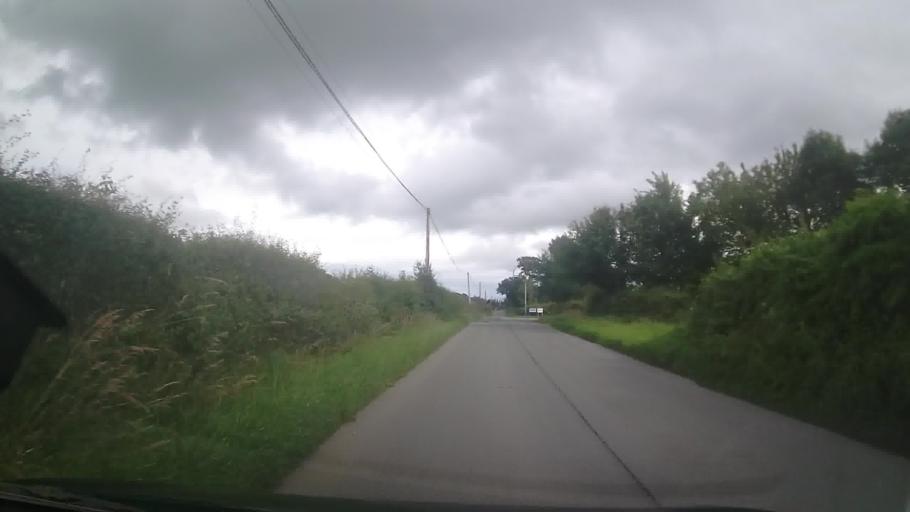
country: GB
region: England
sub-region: Shropshire
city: Whitchurch
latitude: 52.9499
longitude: -2.7351
